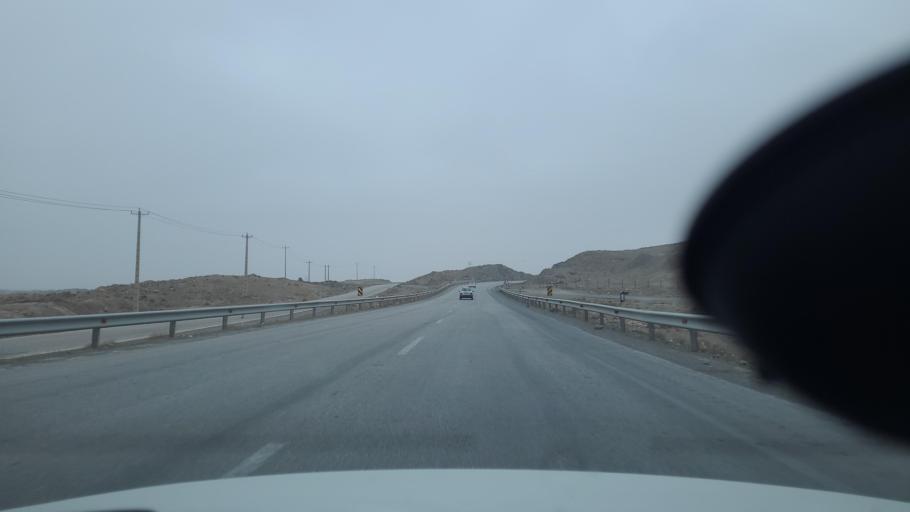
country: IR
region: Razavi Khorasan
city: Fariman
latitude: 35.9959
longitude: 59.7573
